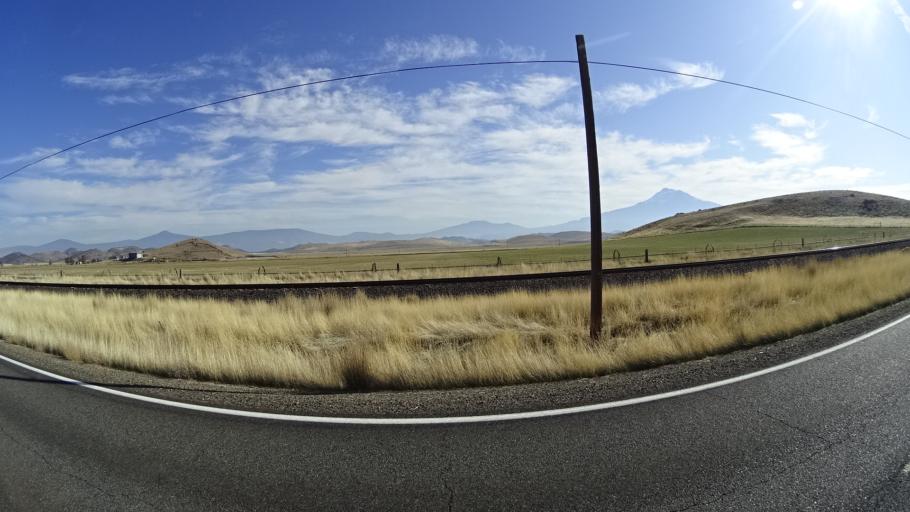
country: US
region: California
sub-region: Siskiyou County
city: Montague
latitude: 41.5569
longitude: -122.5269
